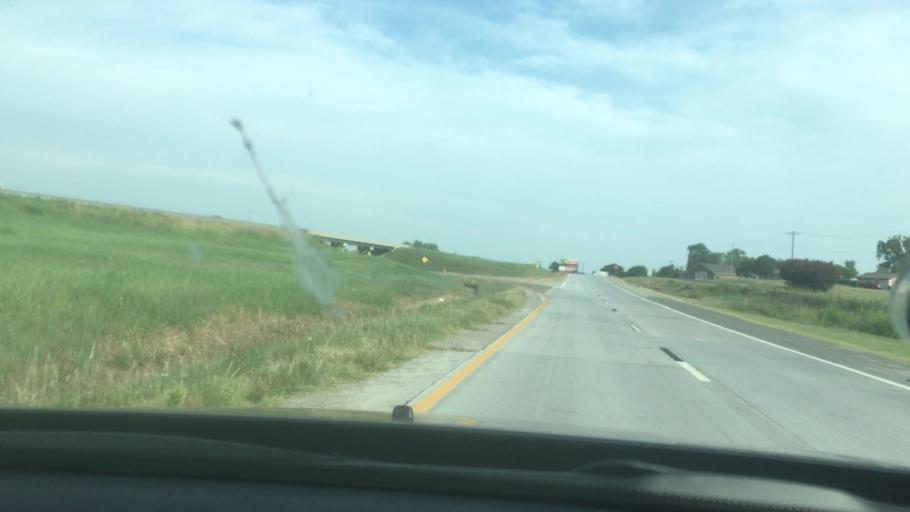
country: US
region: Oklahoma
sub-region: Pontotoc County
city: Ada
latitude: 34.7849
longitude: -96.7230
